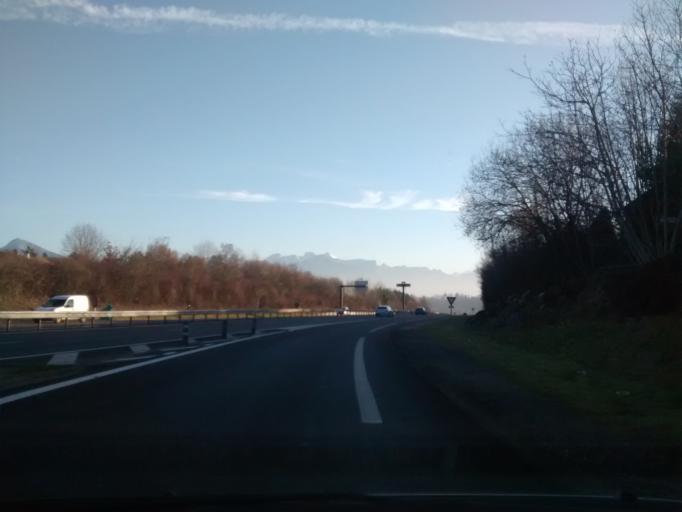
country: FR
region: Rhone-Alpes
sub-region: Departement de la Haute-Savoie
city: Lucinges
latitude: 46.1810
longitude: 6.3056
